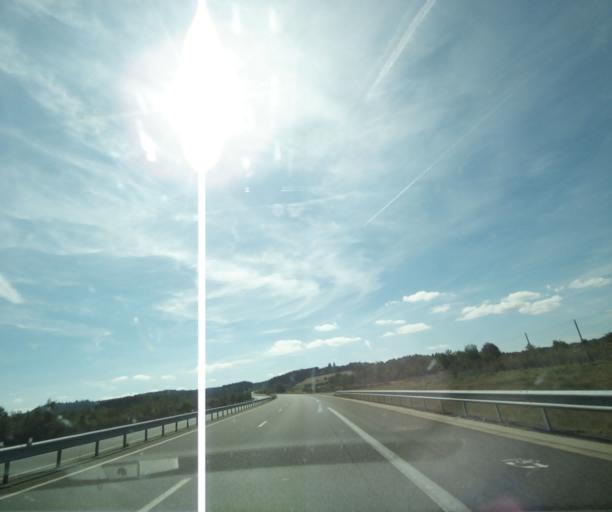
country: FR
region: Auvergne
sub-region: Departement du Puy-de-Dome
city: Gelles
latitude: 45.7686
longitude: 2.7316
